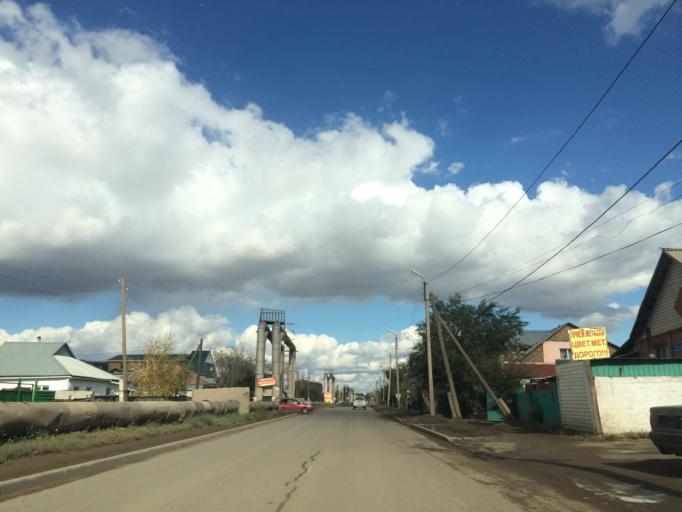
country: KZ
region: Astana Qalasy
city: Astana
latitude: 51.1862
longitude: 71.3897
